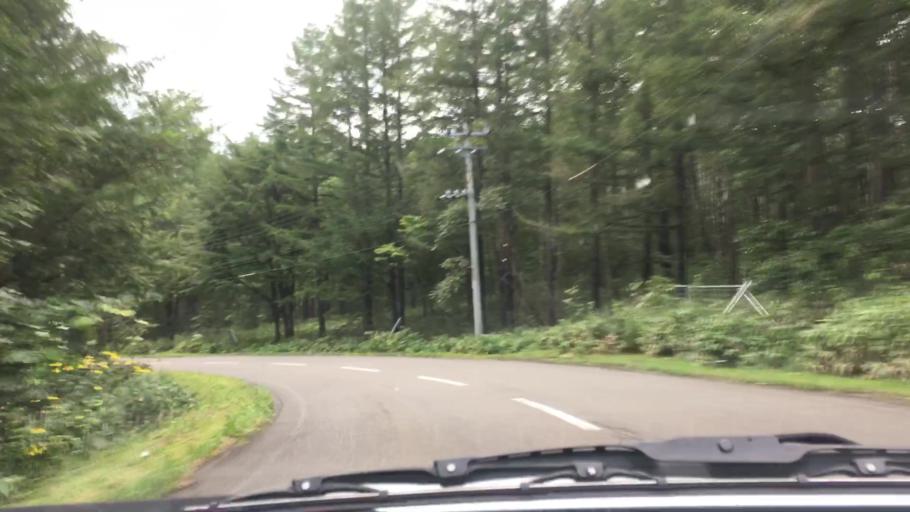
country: JP
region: Hokkaido
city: Otofuke
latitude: 43.1553
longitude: 142.8577
